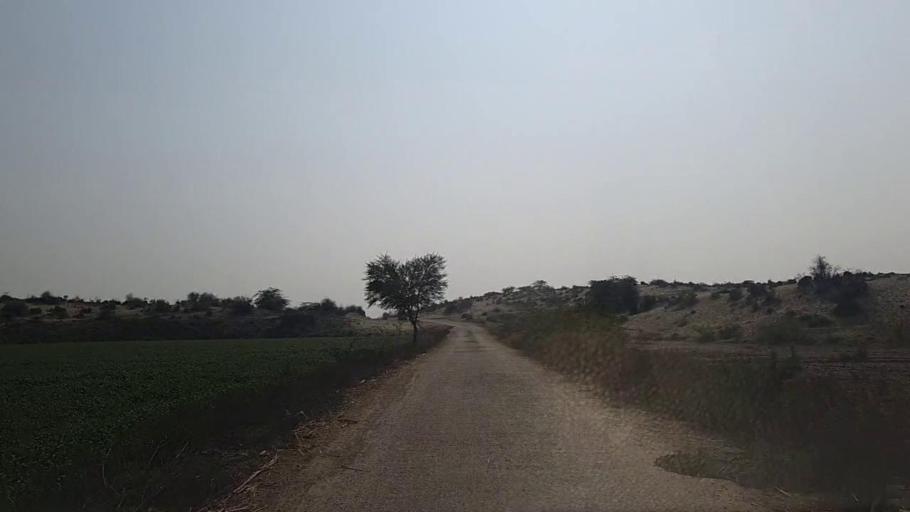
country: PK
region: Sindh
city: Jam Sahib
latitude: 26.4463
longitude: 68.5233
